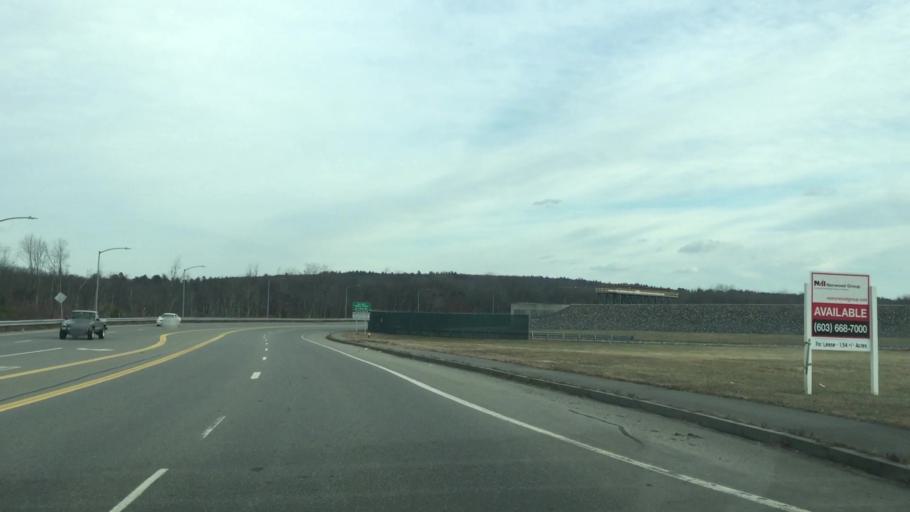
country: US
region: New Hampshire
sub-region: Hillsborough County
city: Manchester
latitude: 42.9457
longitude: -71.4310
